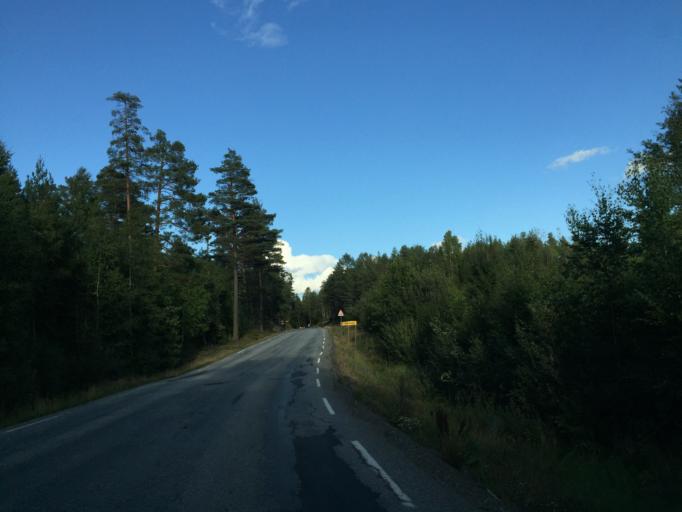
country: NO
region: Ostfold
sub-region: Trogstad
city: Skjonhaug
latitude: 59.6449
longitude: 11.3350
